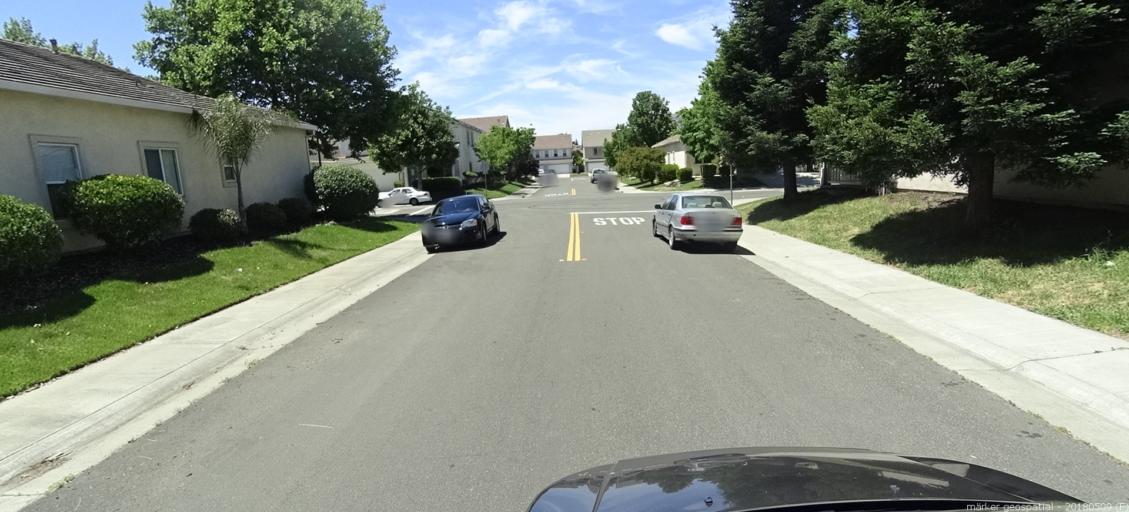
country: US
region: California
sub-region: Sacramento County
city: Sacramento
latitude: 38.6367
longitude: -121.5091
